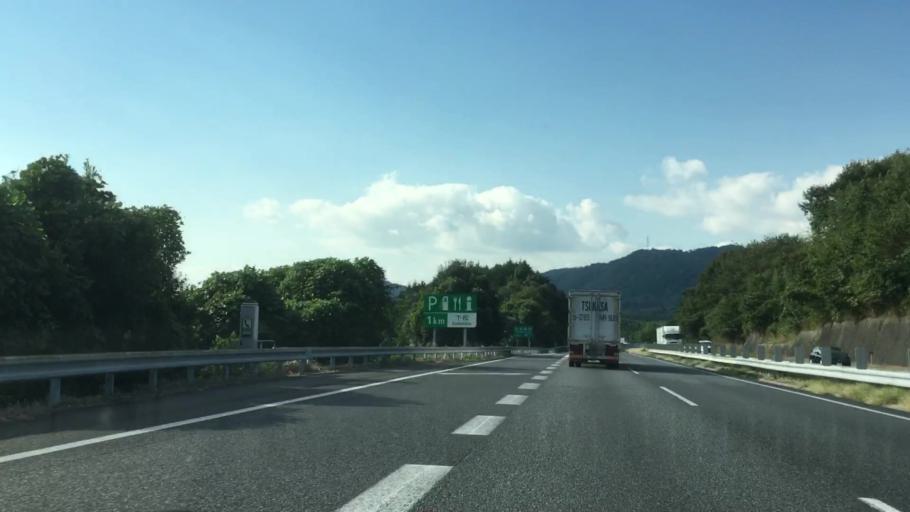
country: JP
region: Yamaguchi
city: Kudamatsu
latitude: 34.0358
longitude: 131.9275
